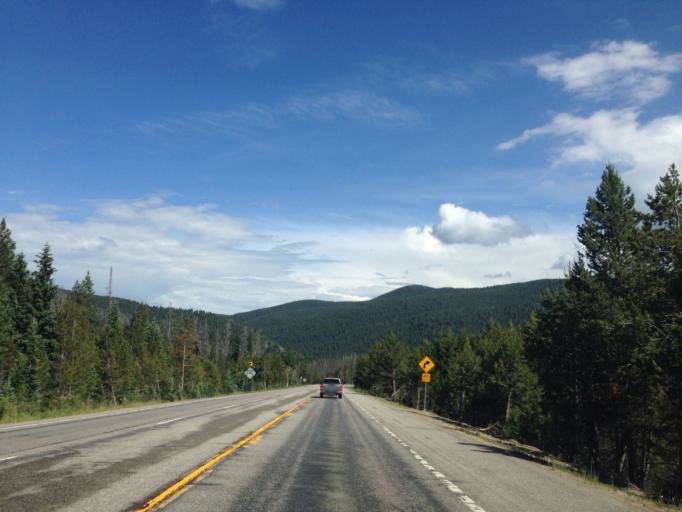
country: US
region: Colorado
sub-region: Routt County
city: Steamboat Springs
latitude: 40.3539
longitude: -106.7477
